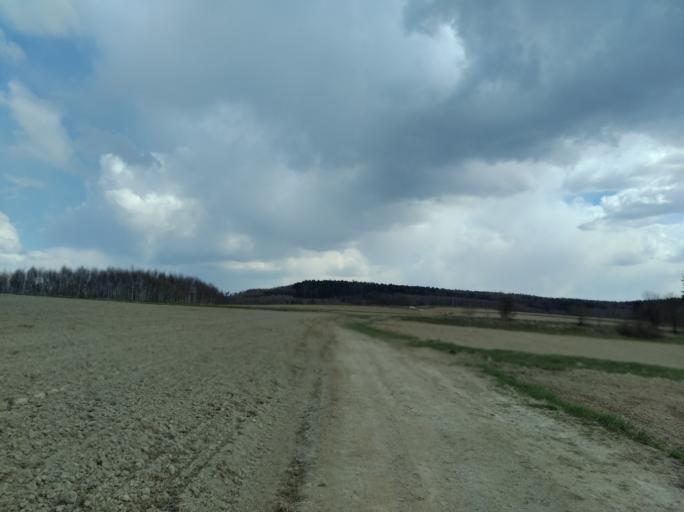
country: PL
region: Subcarpathian Voivodeship
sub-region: Powiat strzyzowski
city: Strzyzow
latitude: 49.9105
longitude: 21.7585
